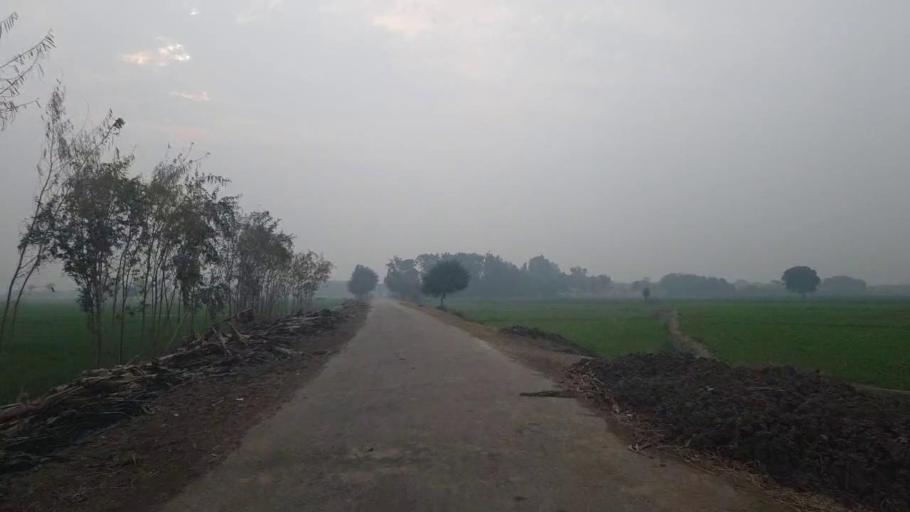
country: PK
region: Sindh
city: Tando Adam
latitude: 25.7348
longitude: 68.6703
